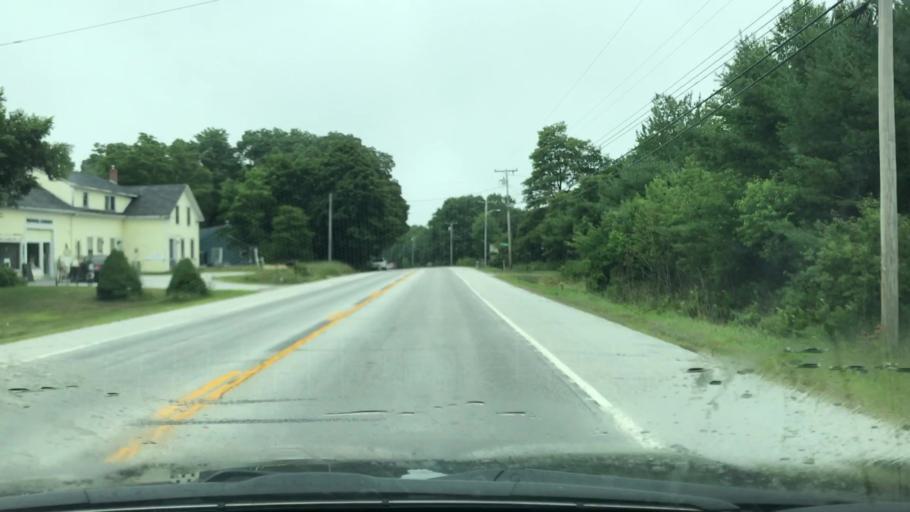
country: US
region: Maine
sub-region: Waldo County
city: Northport
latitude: 44.3285
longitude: -68.9587
